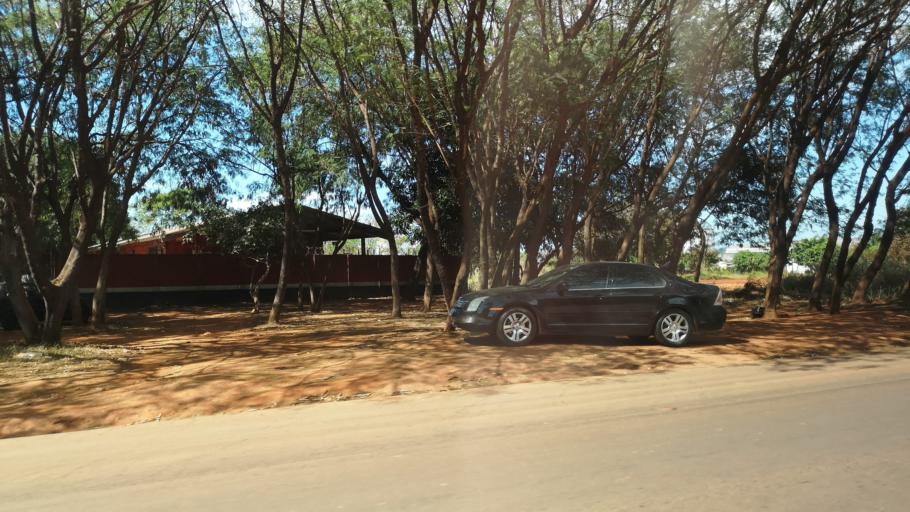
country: BR
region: Goias
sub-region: Senador Canedo
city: Senador Canedo
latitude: -16.7107
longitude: -49.1110
